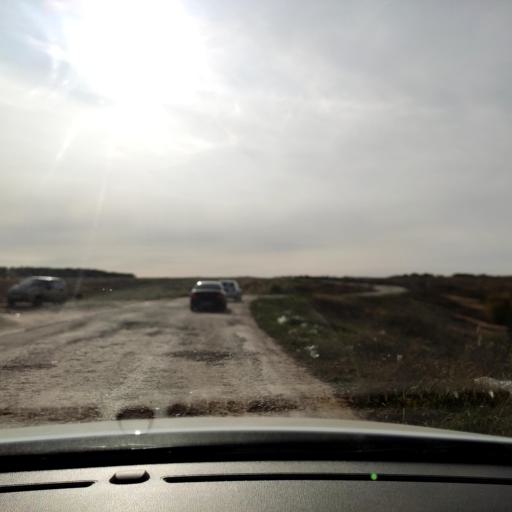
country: RU
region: Tatarstan
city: Vysokaya Gora
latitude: 55.8624
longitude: 49.3644
